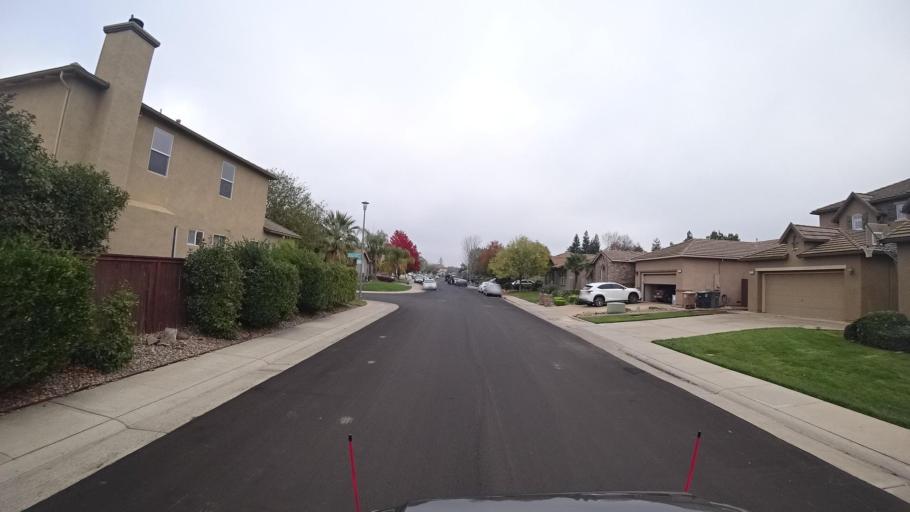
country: US
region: California
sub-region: Sacramento County
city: Elk Grove
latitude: 38.3922
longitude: -121.3474
